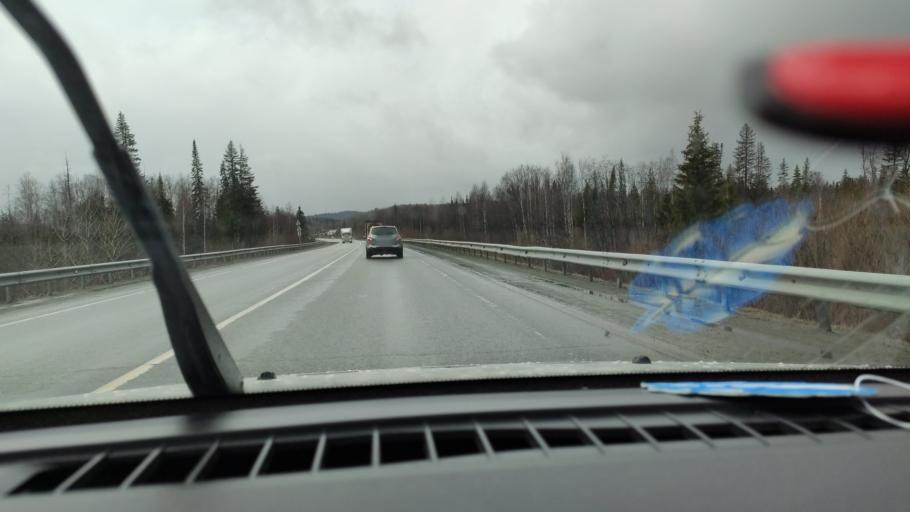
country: RU
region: Sverdlovsk
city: Arti
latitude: 56.7961
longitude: 58.6225
